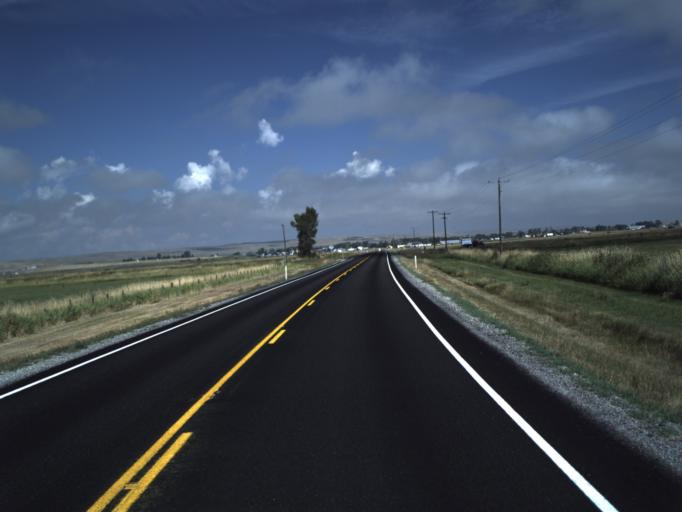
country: US
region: Utah
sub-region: Rich County
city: Randolph
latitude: 41.6419
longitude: -111.1831
